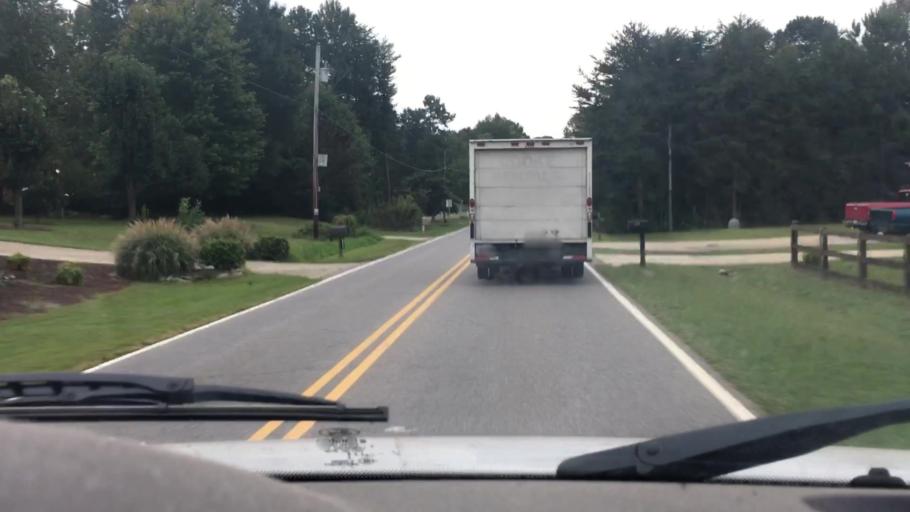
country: US
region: North Carolina
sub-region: Catawba County
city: Lake Norman of Catawba
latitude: 35.5592
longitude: -80.9905
